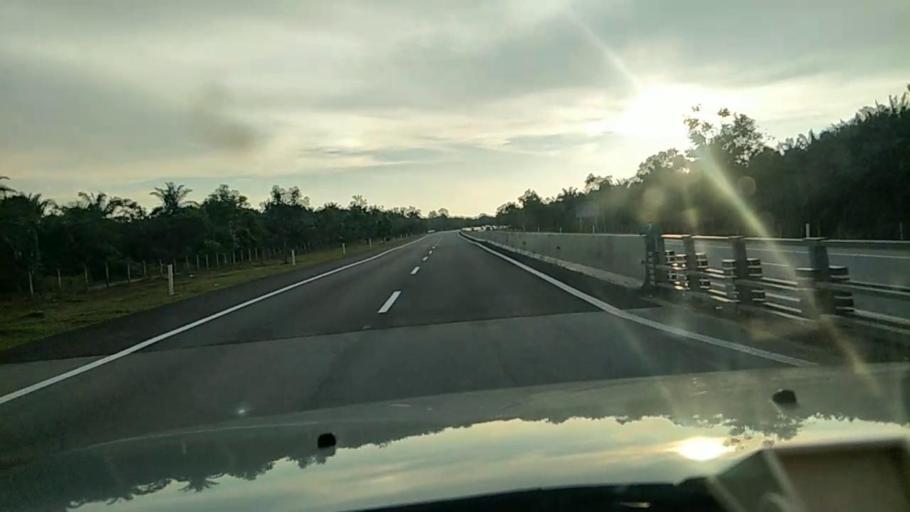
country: MY
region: Selangor
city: Batu Arang
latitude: 3.2877
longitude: 101.4222
